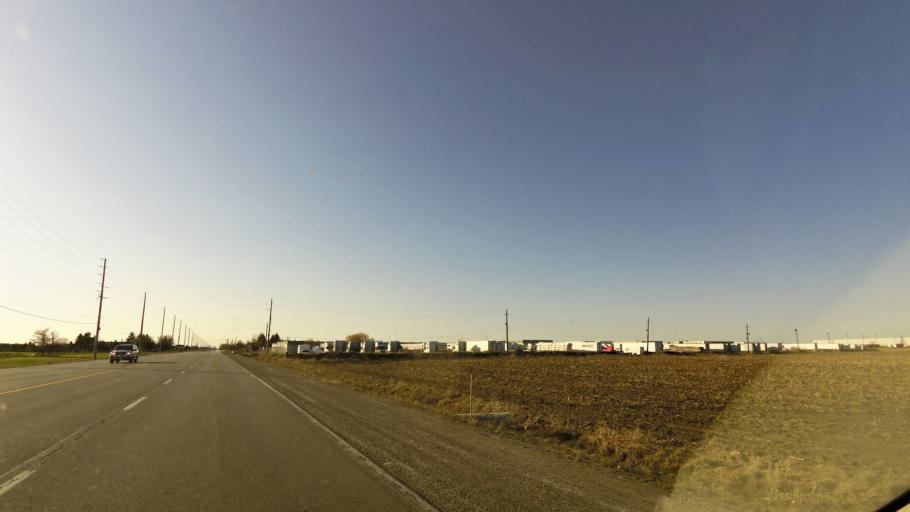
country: CA
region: Ontario
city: Brampton
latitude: 43.8411
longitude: -79.7085
